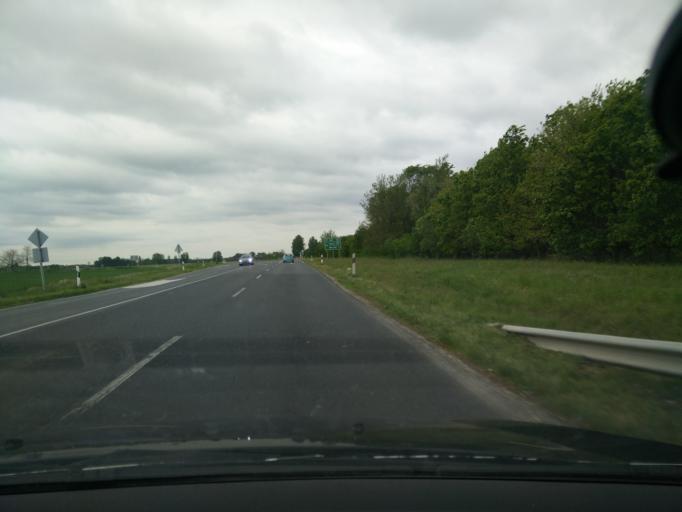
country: HU
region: Veszprem
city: Papa
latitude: 47.3632
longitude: 17.4588
